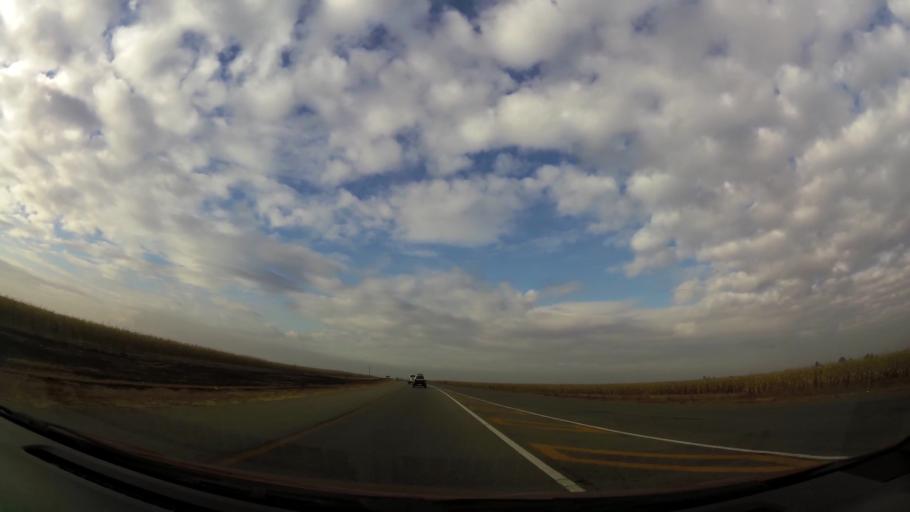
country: ZA
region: Gauteng
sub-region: Sedibeng District Municipality
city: Vanderbijlpark
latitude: -26.6368
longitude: 27.7741
